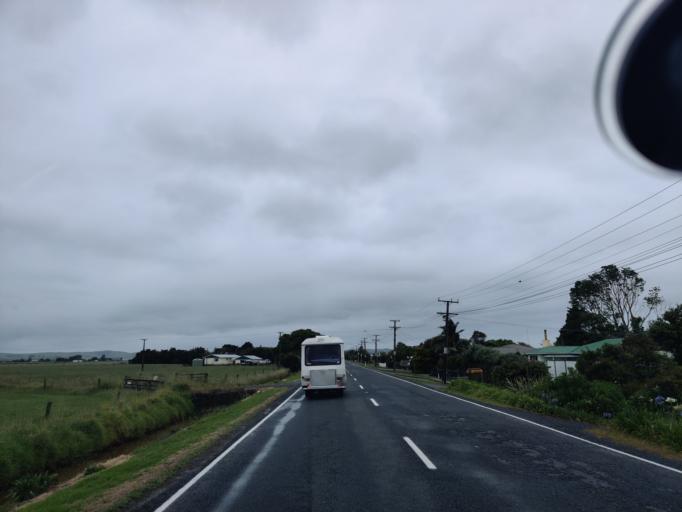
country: NZ
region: Northland
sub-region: Kaipara District
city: Dargaville
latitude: -36.1321
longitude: 174.0305
